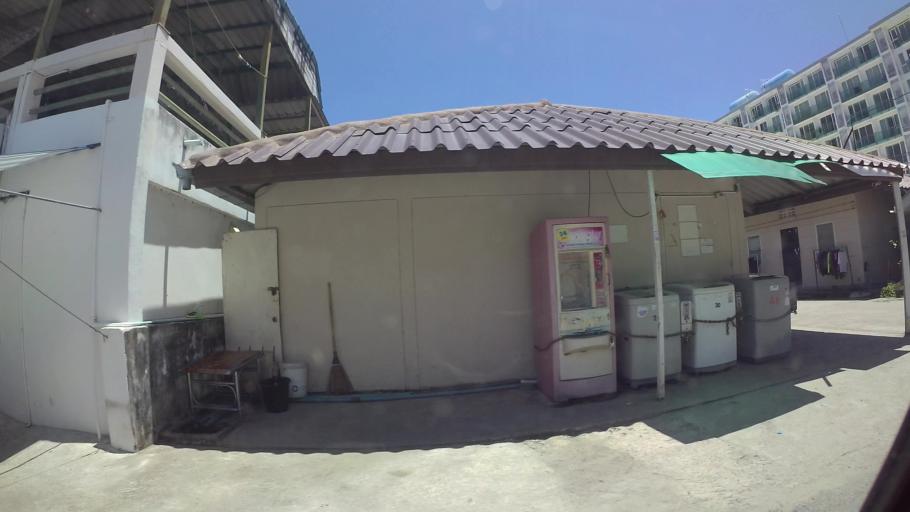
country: TH
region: Chon Buri
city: Phatthaya
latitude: 12.9276
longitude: 100.8897
